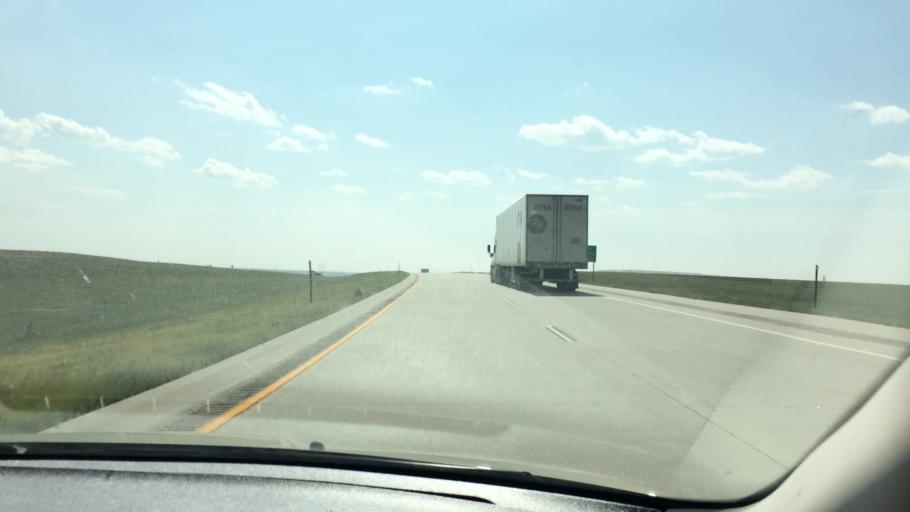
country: US
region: Colorado
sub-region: Lincoln County
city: Limon
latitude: 39.2669
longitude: -103.6315
